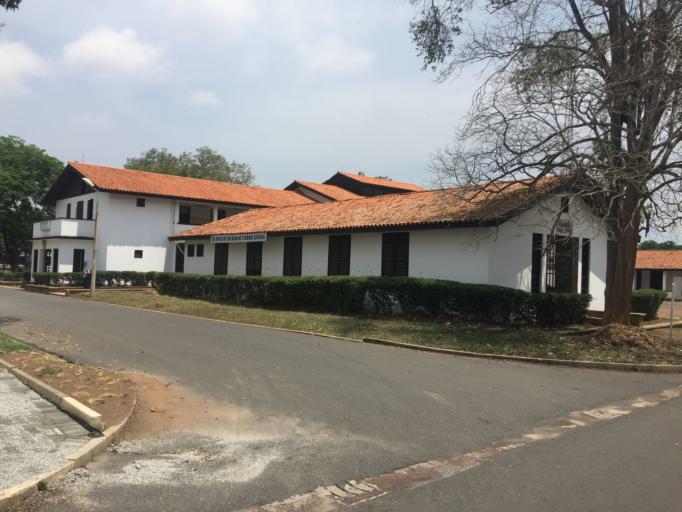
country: GH
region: Greater Accra
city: Medina Estates
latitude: 5.6515
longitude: -0.1879
